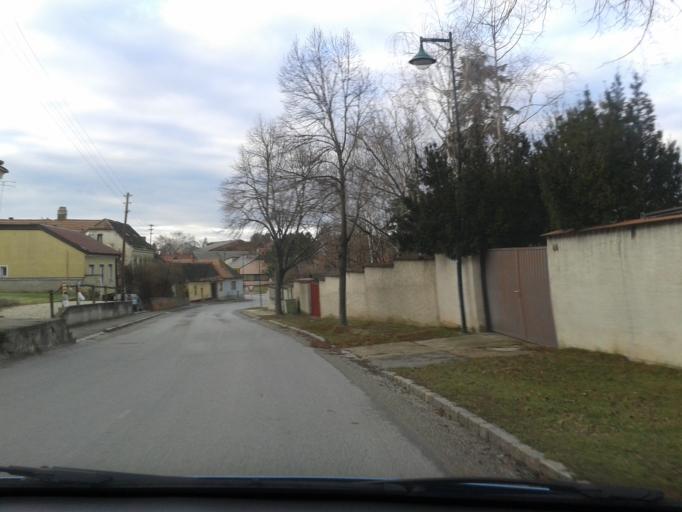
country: AT
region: Lower Austria
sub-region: Politischer Bezirk Ganserndorf
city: Drosing
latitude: 48.5596
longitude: 16.8741
